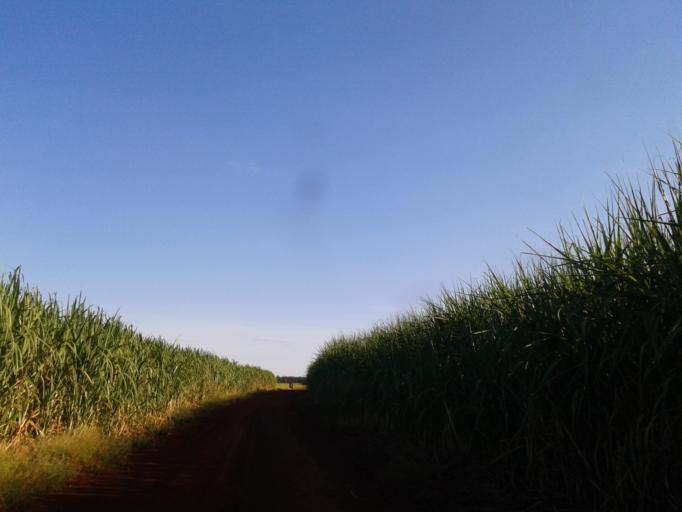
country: BR
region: Minas Gerais
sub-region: Centralina
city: Centralina
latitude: -18.6647
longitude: -49.2709
